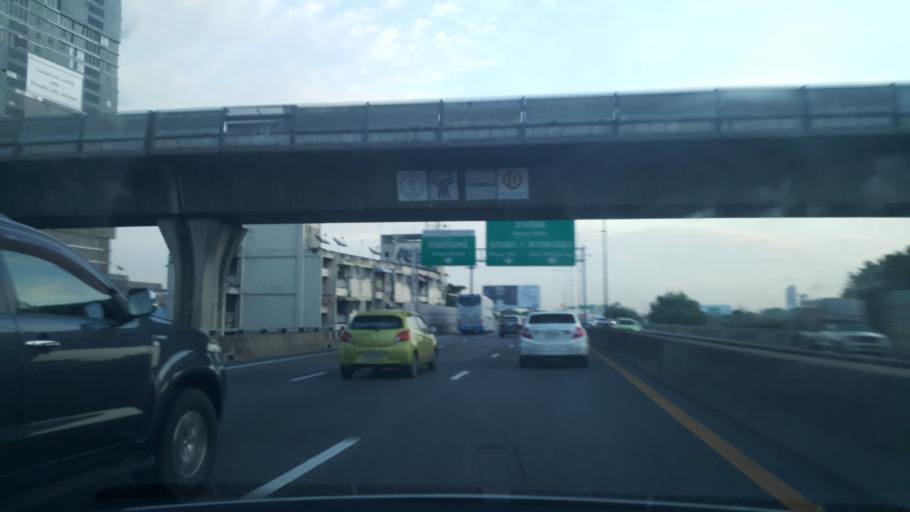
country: TH
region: Bangkok
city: Sathon
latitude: 13.7189
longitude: 100.5189
